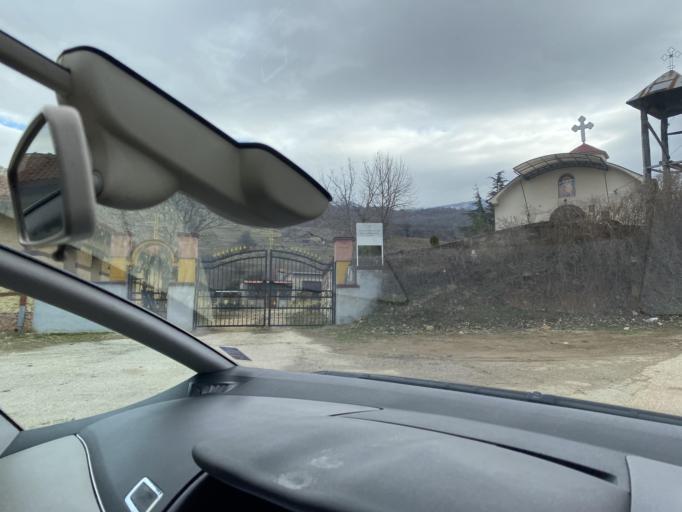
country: MK
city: Radishani
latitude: 42.1070
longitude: 21.4555
